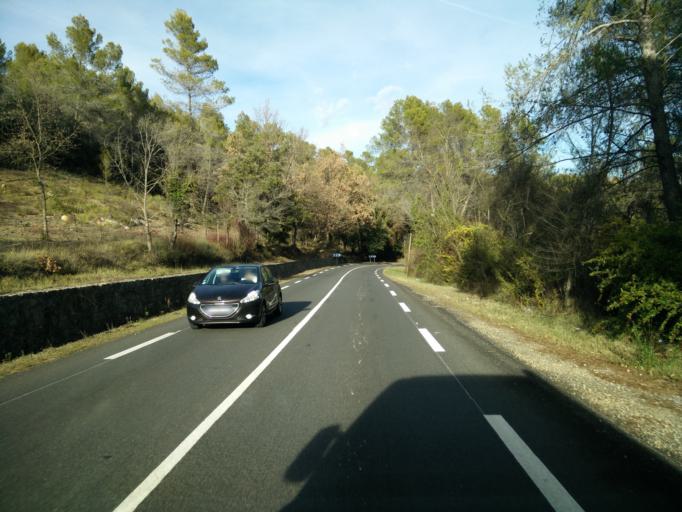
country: FR
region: Provence-Alpes-Cote d'Azur
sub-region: Departement du Var
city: Montauroux
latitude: 43.6078
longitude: 6.8099
